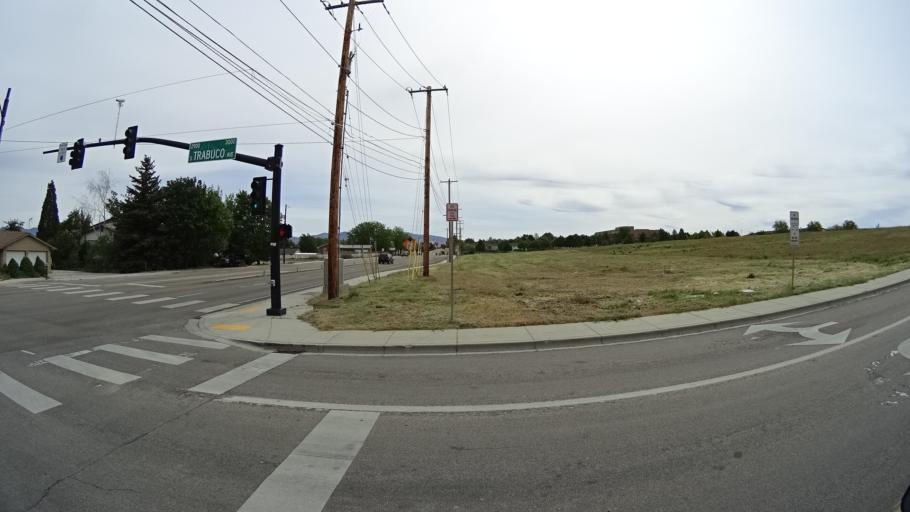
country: US
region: Idaho
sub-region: Ada County
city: Garden City
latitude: 43.5755
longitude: -116.2867
